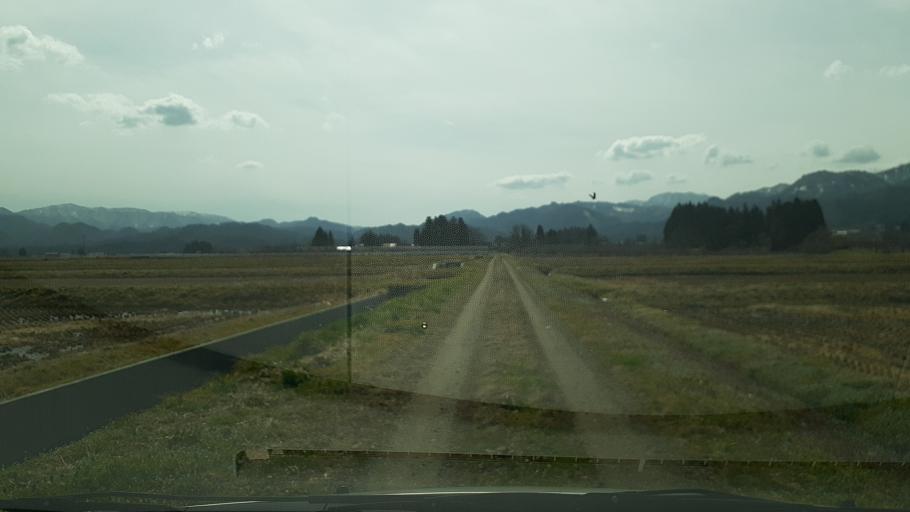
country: JP
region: Fukushima
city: Kitakata
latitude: 37.4578
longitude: 139.8266
